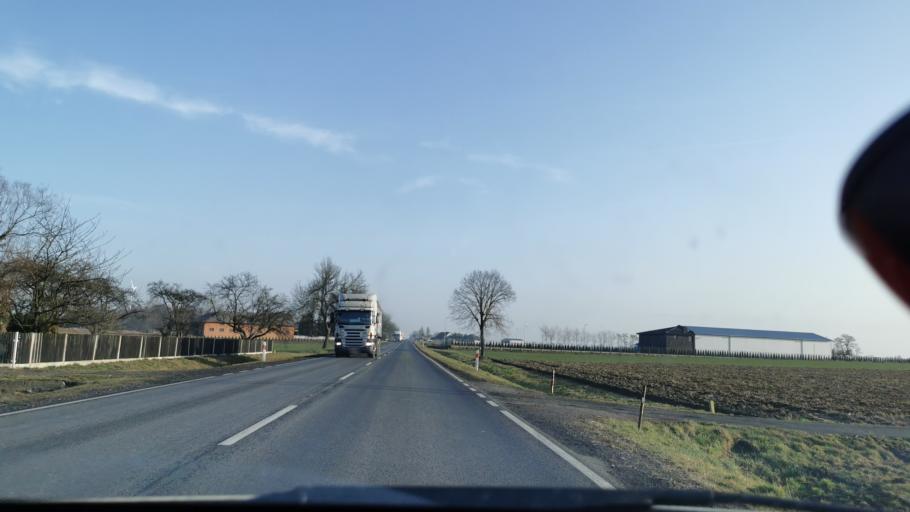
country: PL
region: Lodz Voivodeship
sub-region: Powiat sieradzki
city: Blaszki
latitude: 51.6768
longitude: 18.3544
